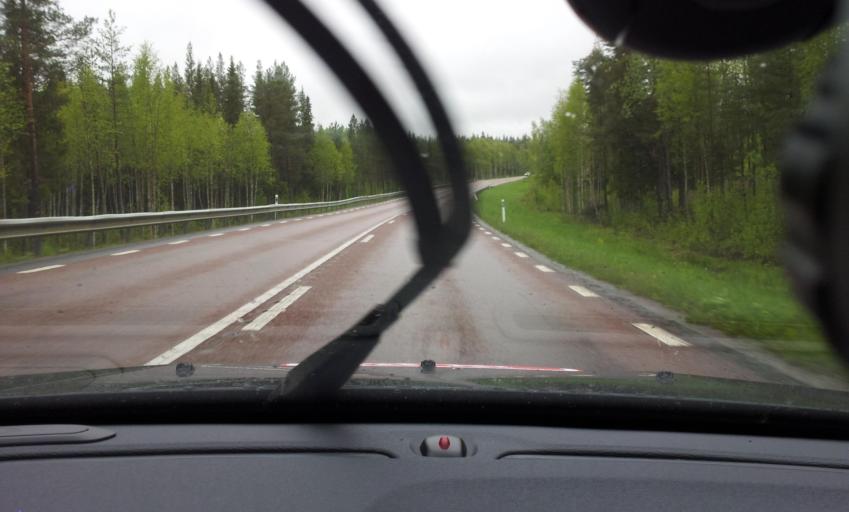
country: SE
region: Jaemtland
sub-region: Bergs Kommun
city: Hoverberg
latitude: 62.8046
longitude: 14.5163
